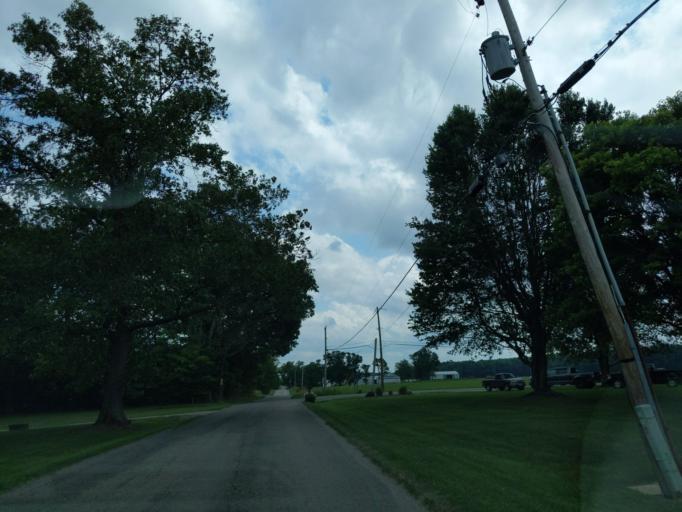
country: US
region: Indiana
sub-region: Ripley County
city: Batesville
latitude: 39.3241
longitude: -85.1898
